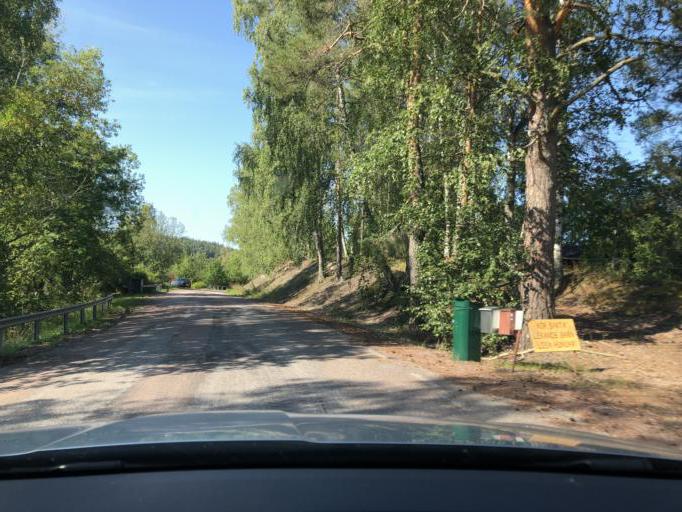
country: SE
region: Dalarna
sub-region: Hedemora Kommun
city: Hedemora
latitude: 60.3466
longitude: 15.9287
